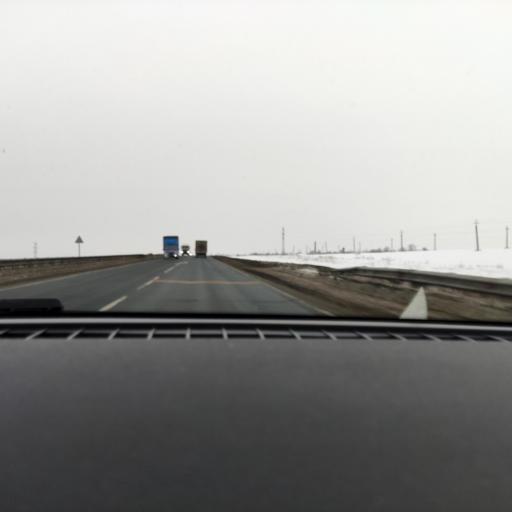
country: RU
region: Samara
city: Smyshlyayevka
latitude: 53.2940
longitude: 50.4598
